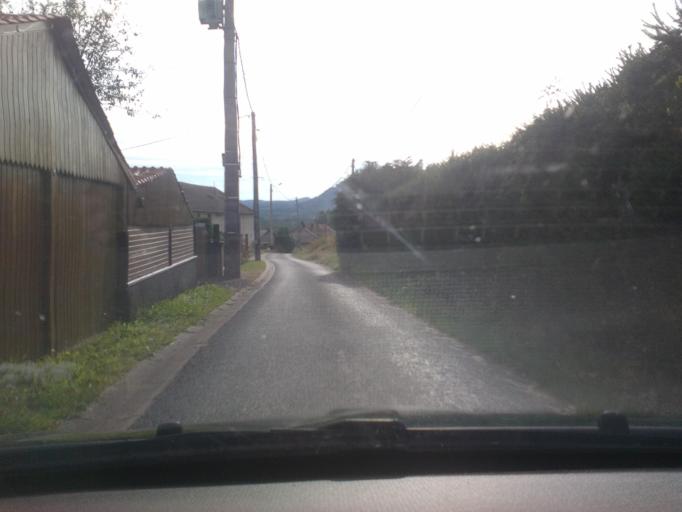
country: FR
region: Lorraine
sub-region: Departement des Vosges
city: Corcieux
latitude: 48.2017
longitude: 6.8808
